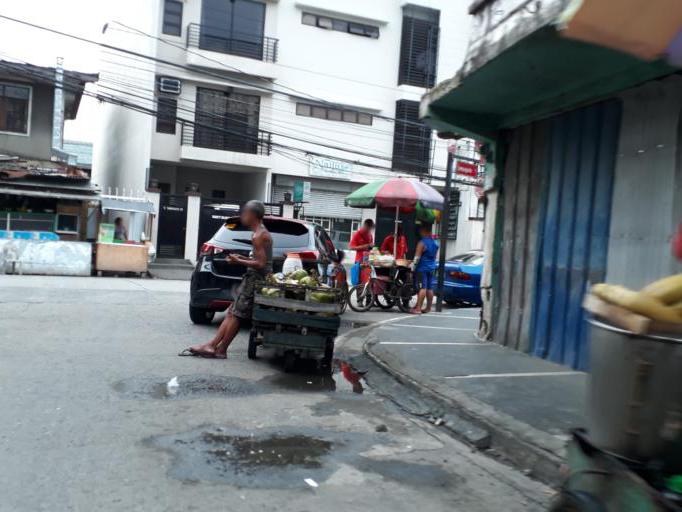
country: PH
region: Calabarzon
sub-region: Province of Rizal
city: Valenzuela
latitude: 14.6784
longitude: 120.9791
